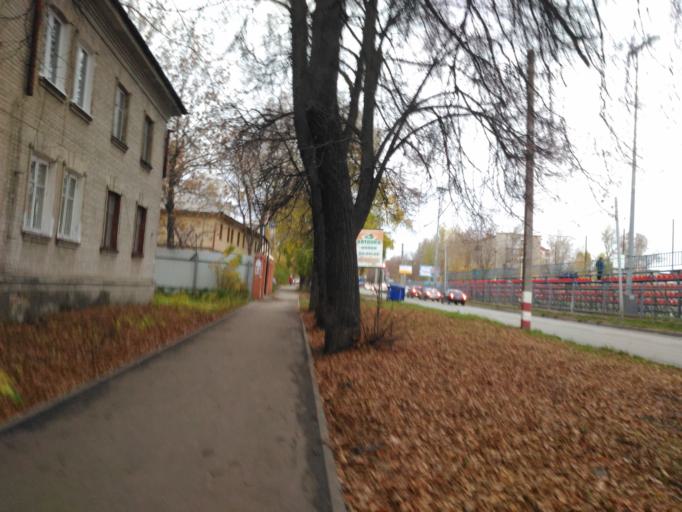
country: RU
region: Ulyanovsk
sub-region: Ulyanovskiy Rayon
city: Ulyanovsk
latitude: 54.3437
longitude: 48.3887
